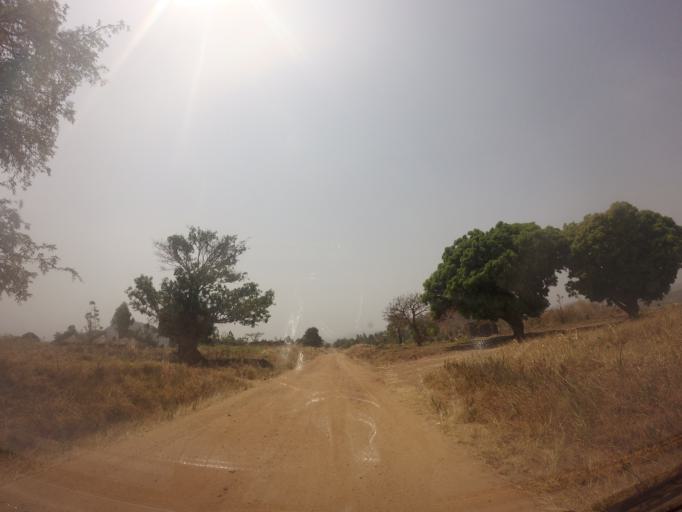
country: UG
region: Northern Region
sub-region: Arua District
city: Arua
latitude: 2.9316
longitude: 30.9824
